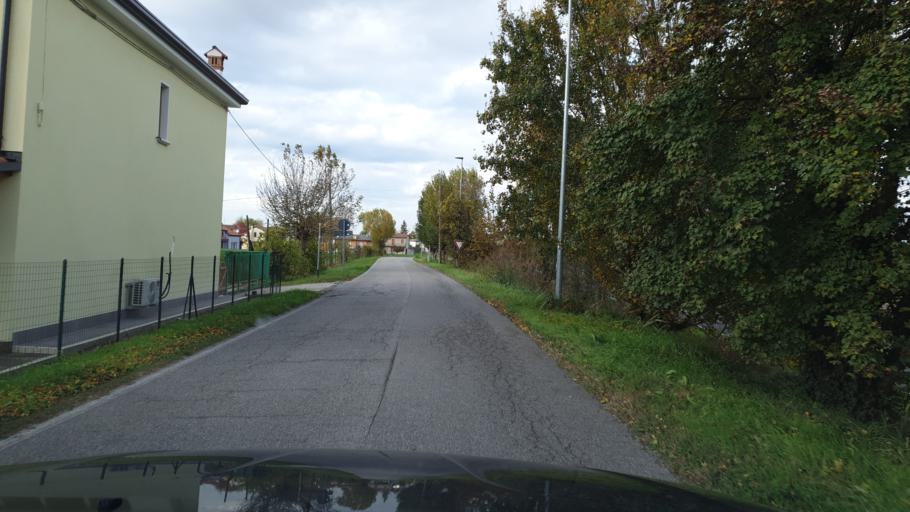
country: IT
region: Veneto
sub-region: Provincia di Rovigo
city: Villanova del Ghebbo Canton
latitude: 45.0452
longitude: 11.6480
